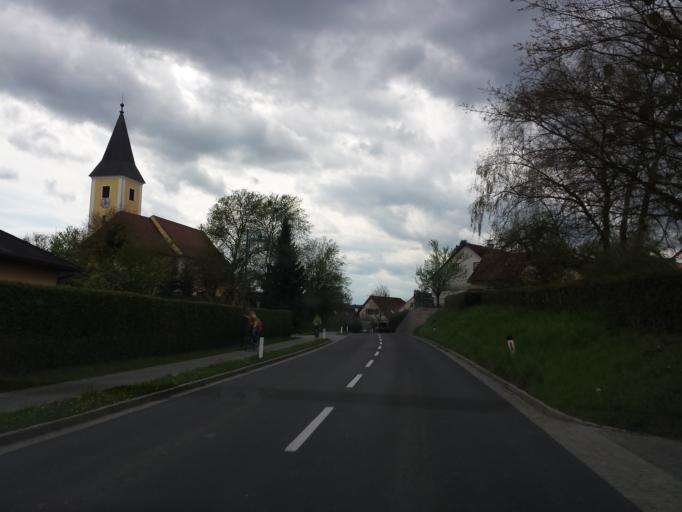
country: AT
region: Styria
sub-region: Politischer Bezirk Hartberg-Fuerstenfeld
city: UEbersbach
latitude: 47.0241
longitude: 16.0578
